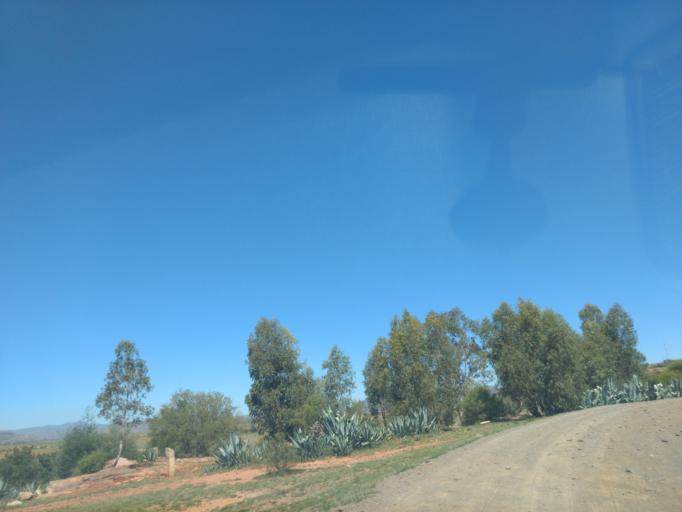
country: LS
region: Maseru
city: Maseru
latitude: -29.4874
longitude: 27.3715
